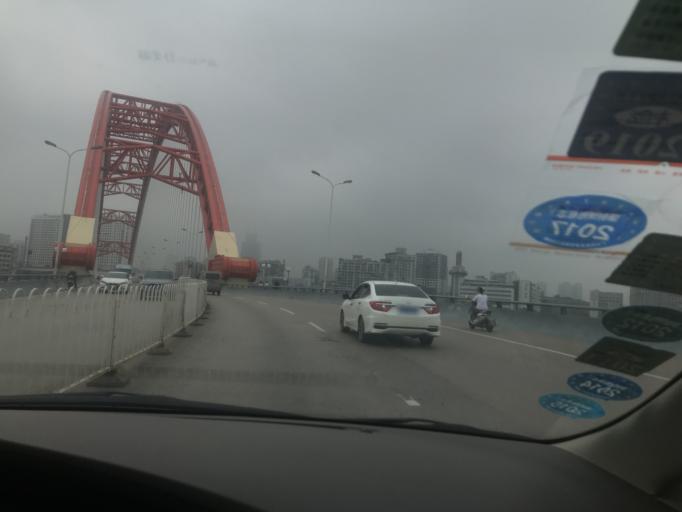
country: CN
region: Hubei
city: Wuhan
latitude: 30.5644
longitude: 114.2805
